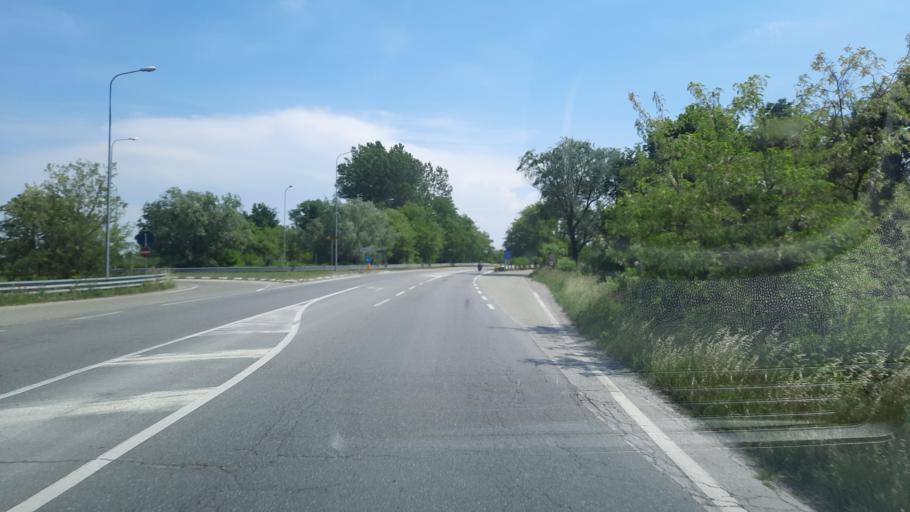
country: IT
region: Lombardy
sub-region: Provincia di Pavia
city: Tromello
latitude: 45.2147
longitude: 8.8577
